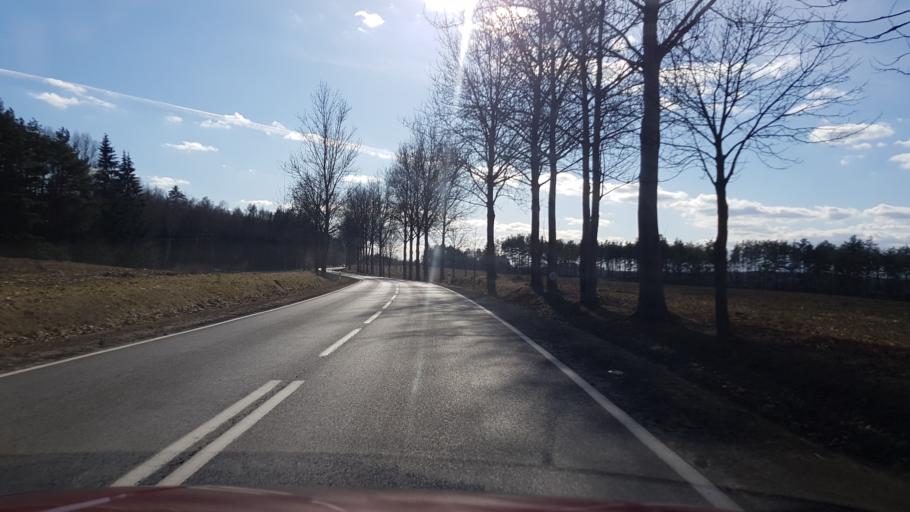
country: PL
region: West Pomeranian Voivodeship
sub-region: Powiat szczecinecki
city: Borne Sulinowo
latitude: 53.6130
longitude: 16.5858
